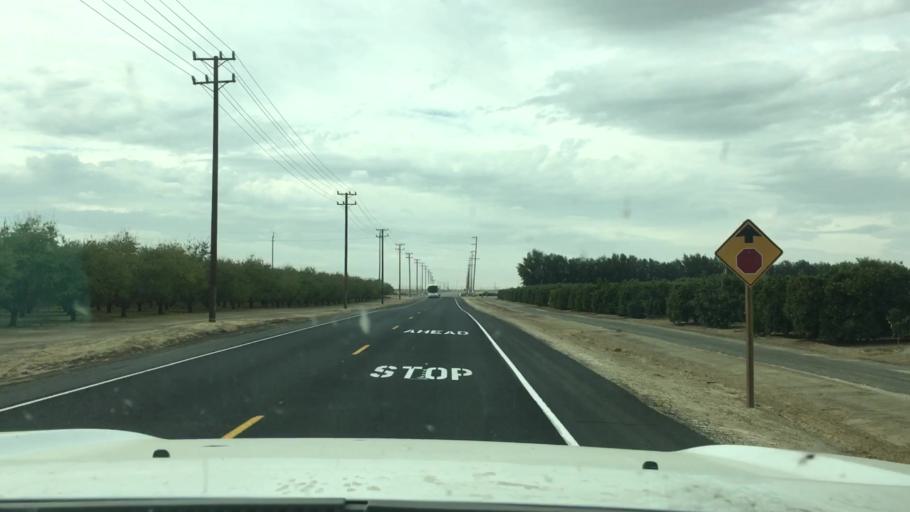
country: US
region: California
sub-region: Kern County
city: Lost Hills
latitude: 35.4991
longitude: -119.7359
